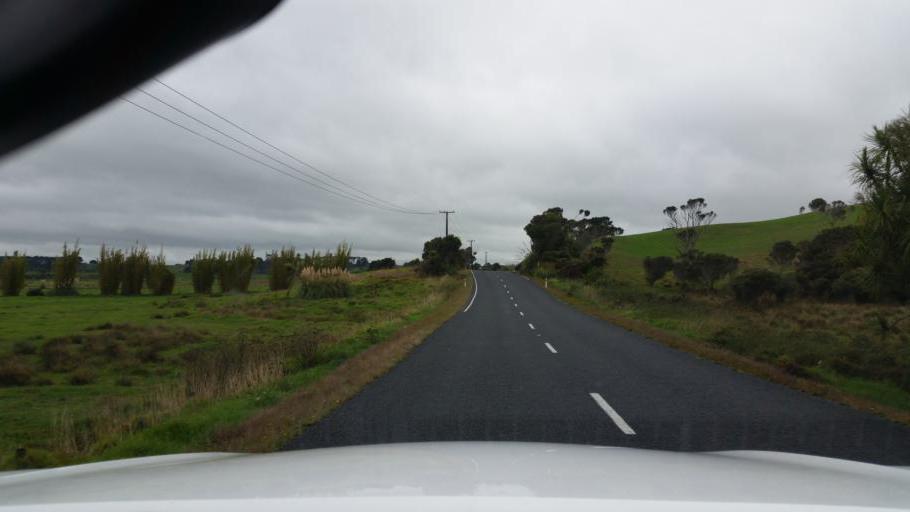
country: NZ
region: Northland
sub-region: Kaipara District
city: Dargaville
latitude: -36.1187
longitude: 173.9595
